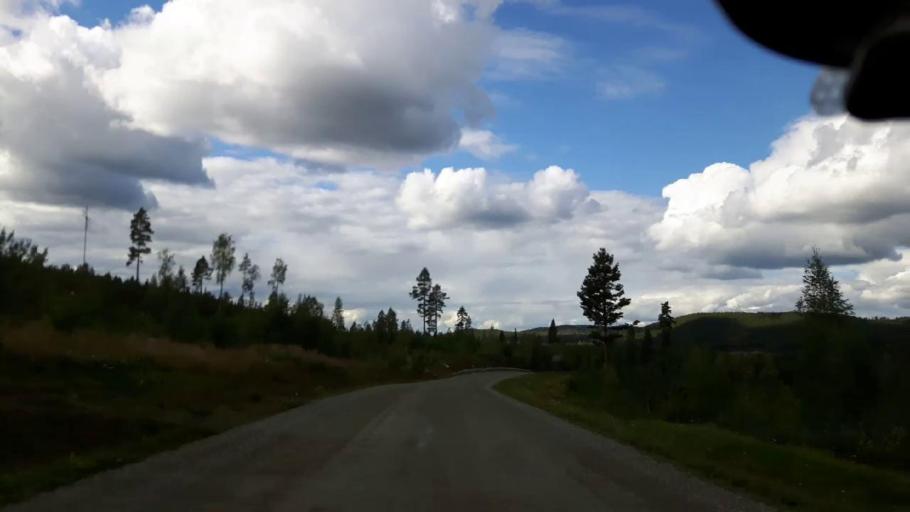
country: SE
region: Jaemtland
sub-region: Stroemsunds Kommun
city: Stroemsund
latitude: 63.4051
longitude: 15.5658
